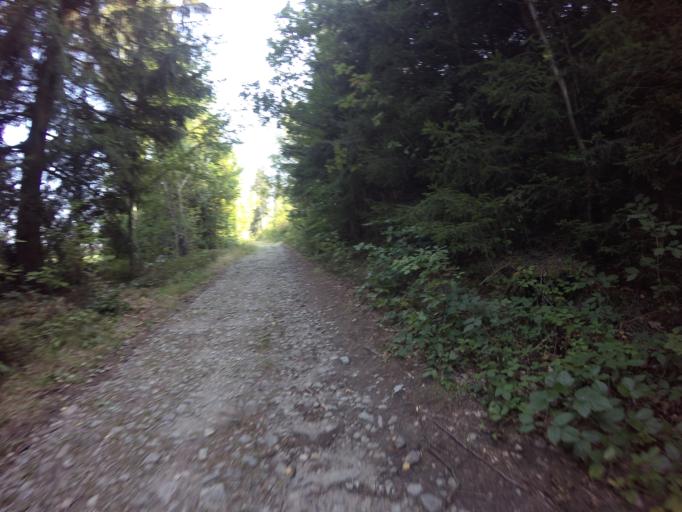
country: AT
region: Upper Austria
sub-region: Politischer Bezirk Urfahr-Umgebung
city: Bad Leonfelden
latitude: 48.5372
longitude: 14.3119
